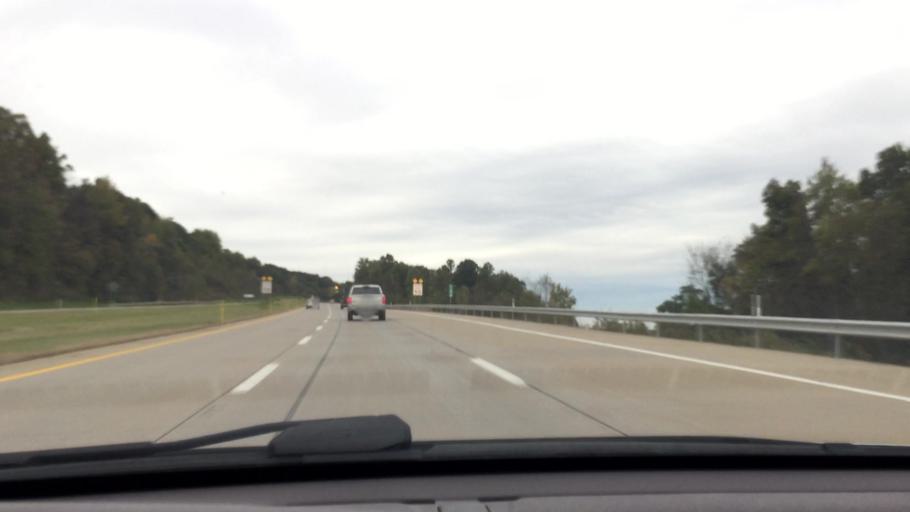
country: US
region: Pennsylvania
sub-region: Lawrence County
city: New Beaver
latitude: 40.9257
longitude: -80.3875
